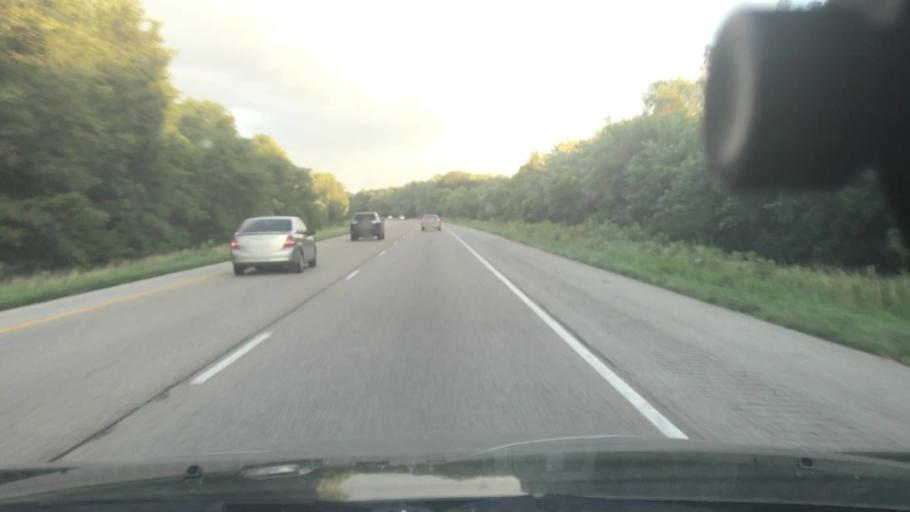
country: US
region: Illinois
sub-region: Clinton County
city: Albers
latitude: 38.4921
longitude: -89.5996
